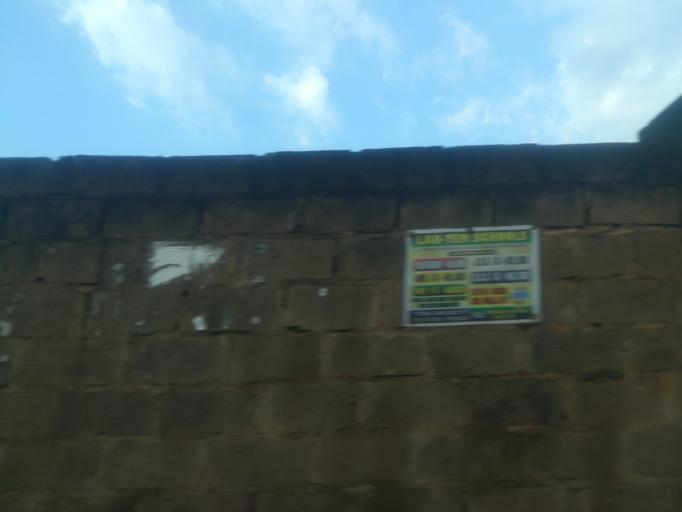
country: NG
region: Oyo
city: Ibadan
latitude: 7.4050
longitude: 3.9459
